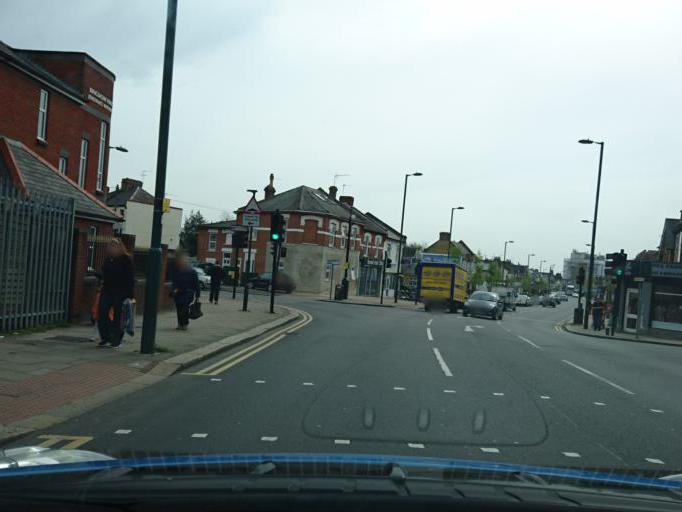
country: GB
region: England
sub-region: Greater London
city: Hadley Wood
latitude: 51.6492
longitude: -0.1699
